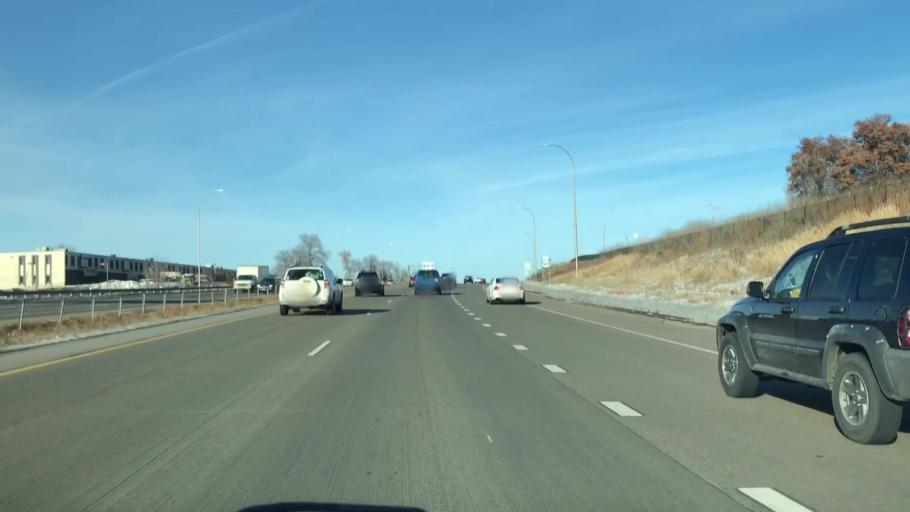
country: US
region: Minnesota
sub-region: Hennepin County
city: Edina
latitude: 44.8660
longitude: -93.3967
